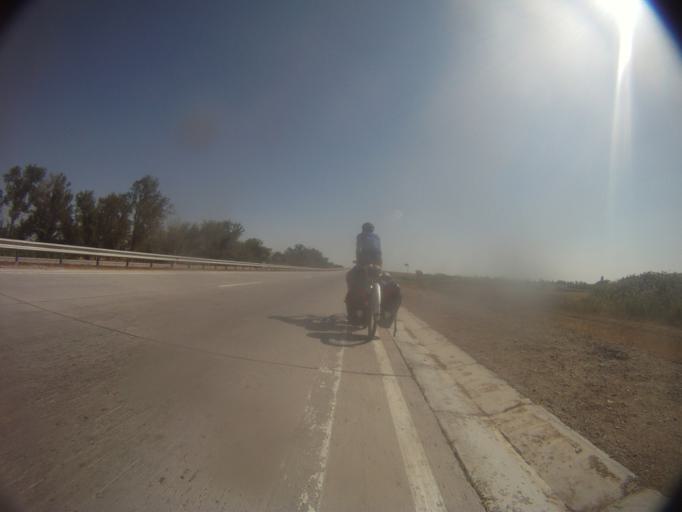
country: KZ
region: Zhambyl
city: Taraz
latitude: 42.7774
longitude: 71.0404
